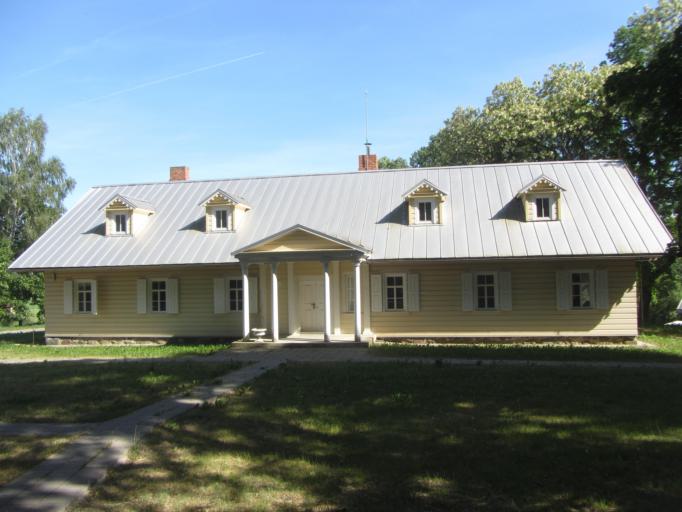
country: LT
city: Birstonas
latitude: 54.5595
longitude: 24.0765
